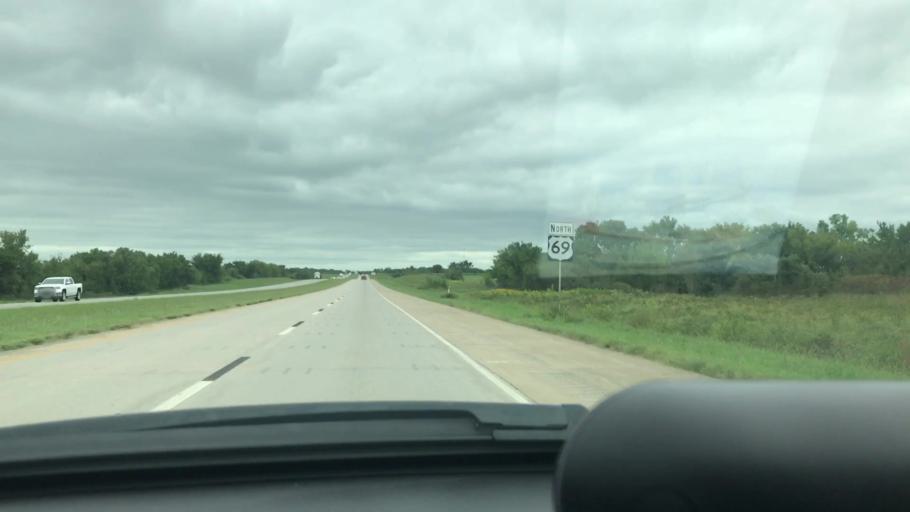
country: US
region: Oklahoma
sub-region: Mayes County
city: Chouteau
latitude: 36.0774
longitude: -95.3644
